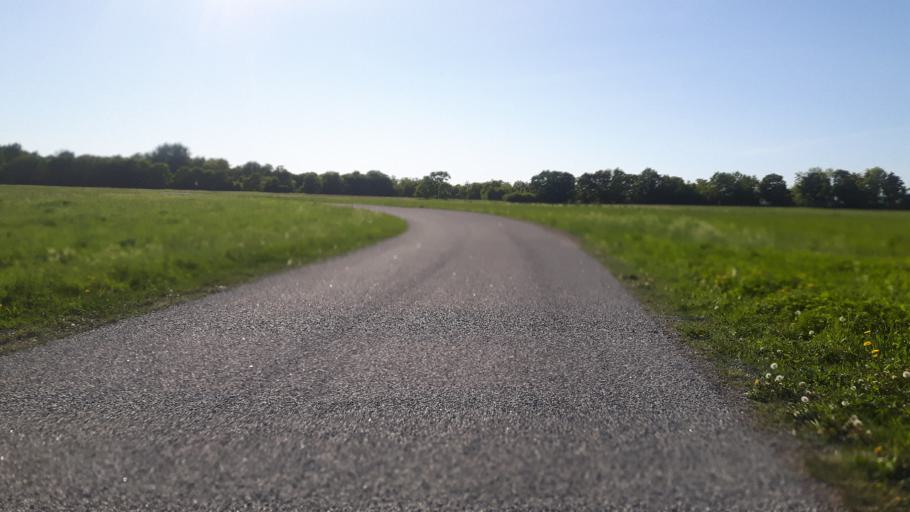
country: EE
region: Ida-Virumaa
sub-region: Kohtla-Nomme vald
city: Kohtla-Nomme
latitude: 59.4386
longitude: 27.1923
